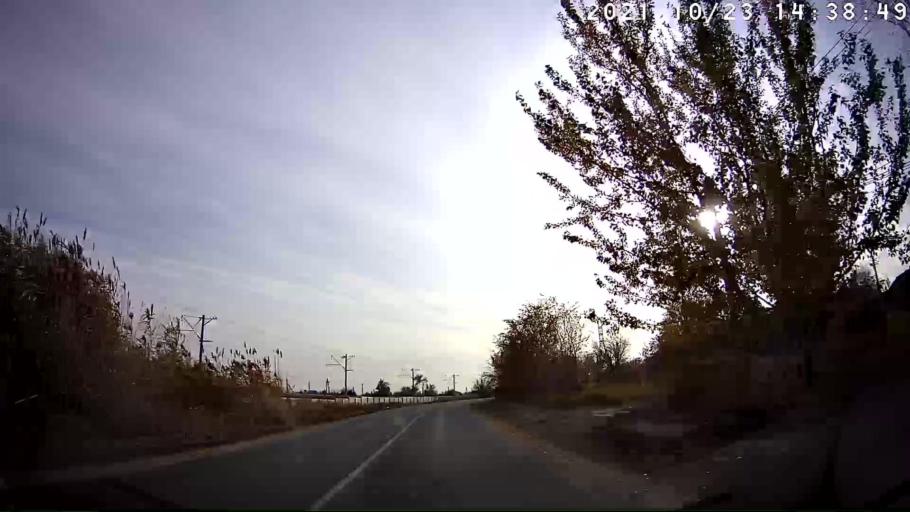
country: RU
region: Volgograd
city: Krasnoslobodsk
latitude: 48.4892
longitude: 44.5486
